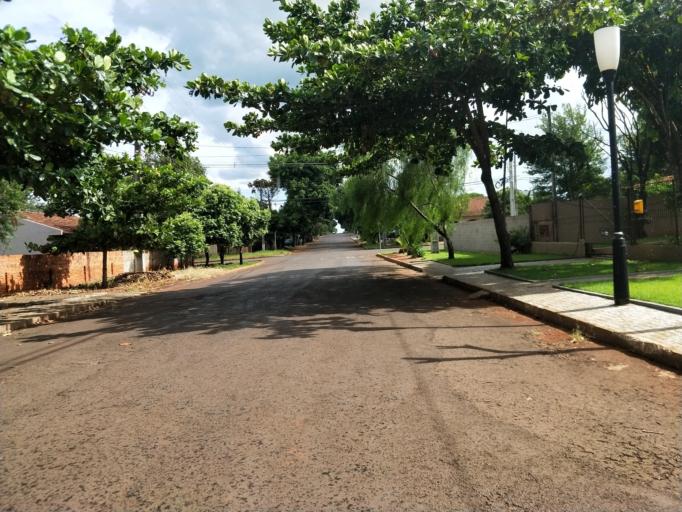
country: BR
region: Parana
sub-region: Marechal Candido Rondon
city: Marechal Candido Rondon
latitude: -24.5563
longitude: -54.0528
